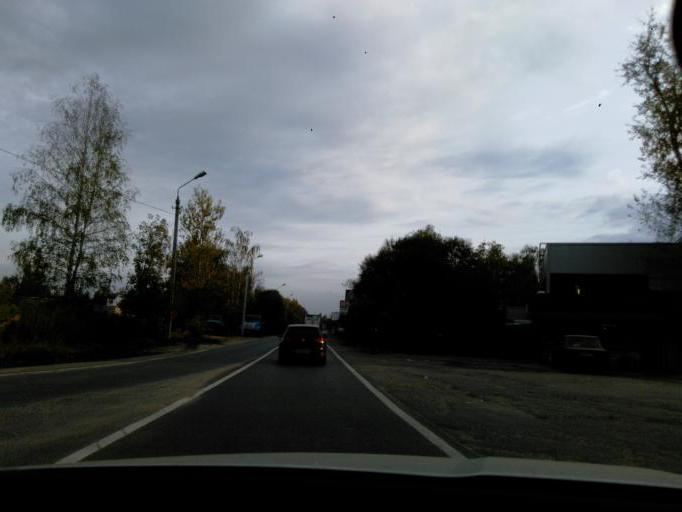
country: RU
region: Moskovskaya
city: Sheremet'yevskiy
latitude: 55.9745
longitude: 37.5216
